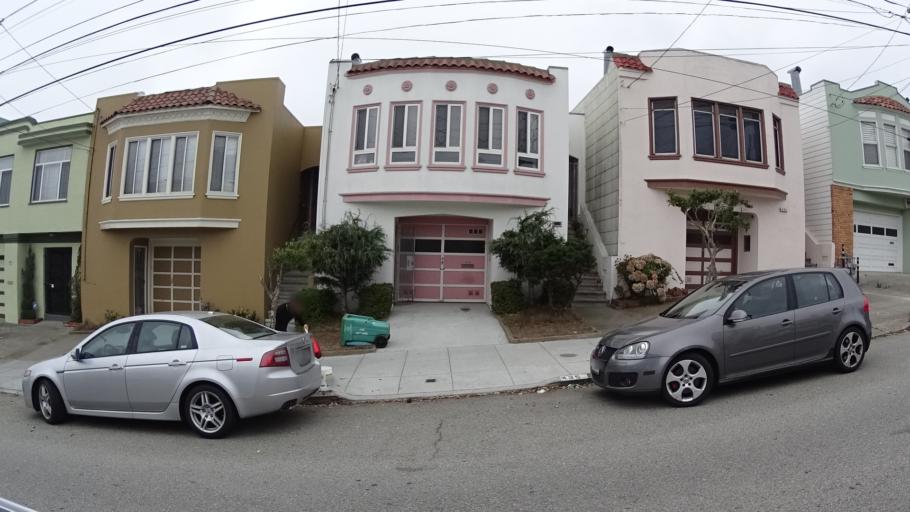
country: US
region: California
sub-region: Marin County
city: Sausalito
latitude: 37.7804
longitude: -122.5030
